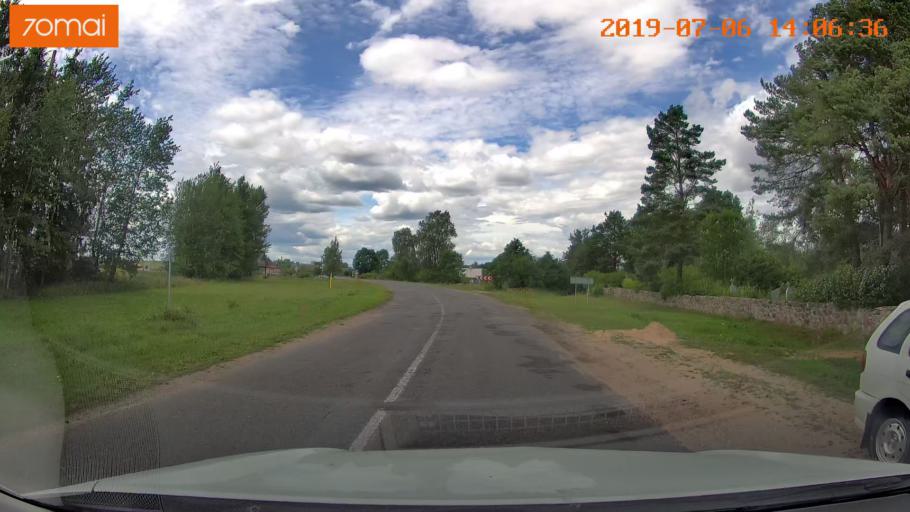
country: BY
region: Minsk
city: Ivyanyets
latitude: 53.8633
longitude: 26.7811
